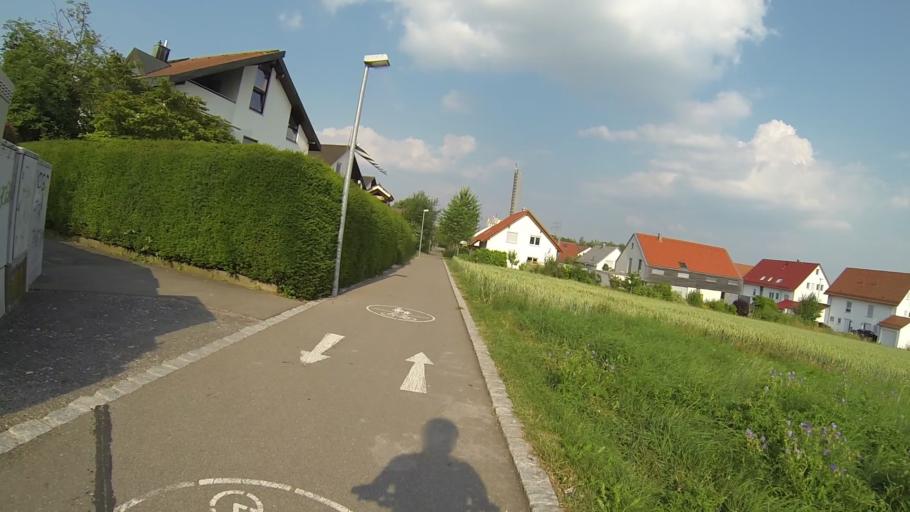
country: DE
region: Baden-Wuerttemberg
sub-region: Tuebingen Region
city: Ulm
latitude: 48.4326
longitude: 9.9737
